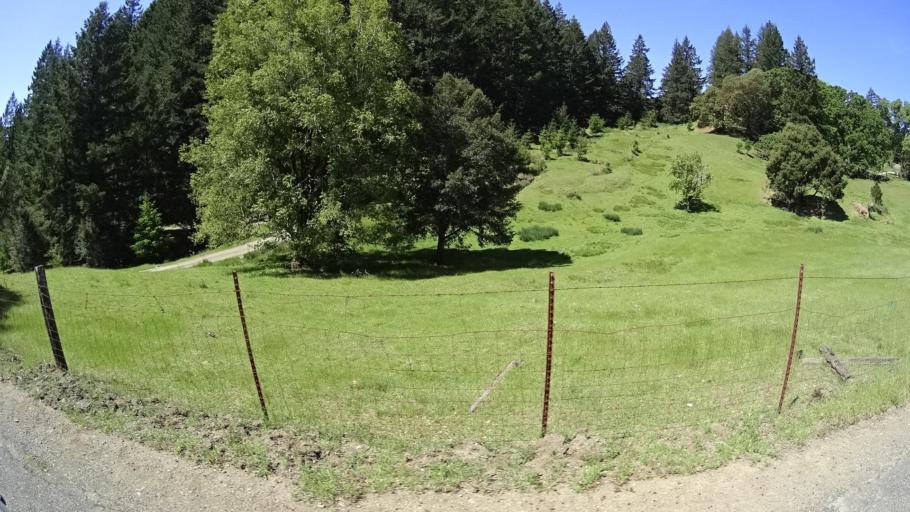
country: US
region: California
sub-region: Humboldt County
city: Redway
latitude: 40.1423
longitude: -124.0057
